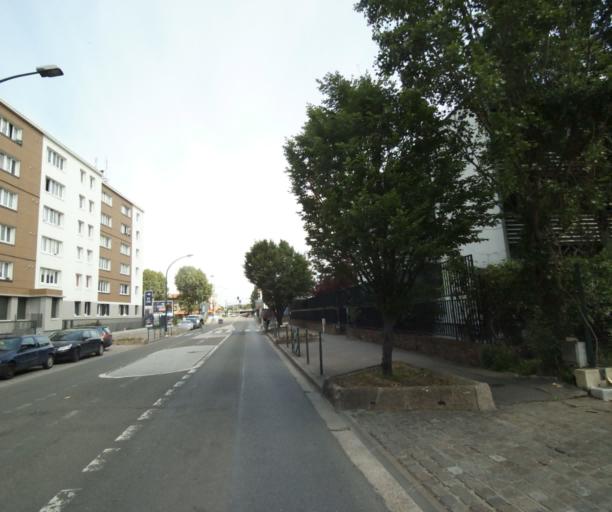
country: FR
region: Ile-de-France
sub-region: Departement des Hauts-de-Seine
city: Colombes
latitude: 48.9310
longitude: 2.2552
